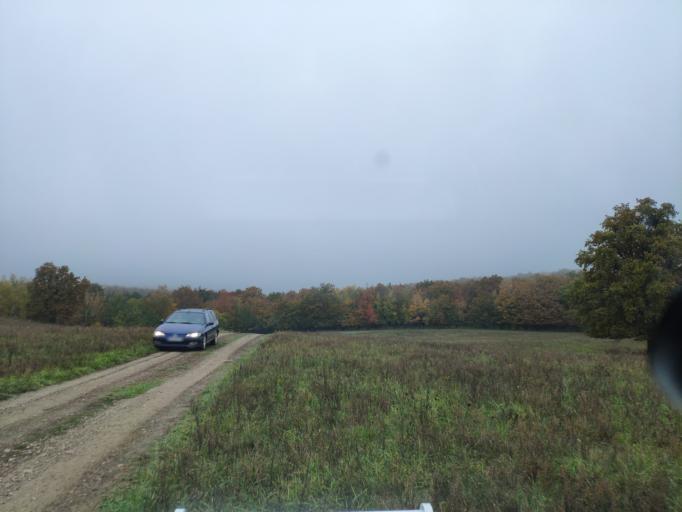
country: SK
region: Kosicky
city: Moldava nad Bodvou
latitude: 48.7137
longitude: 21.0132
